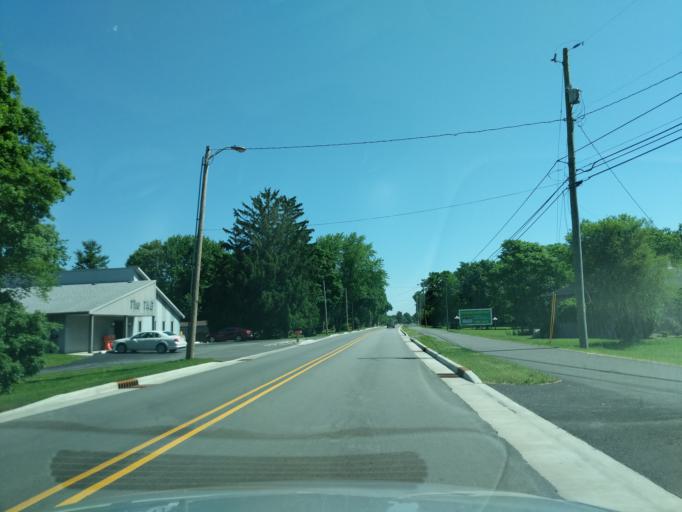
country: US
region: Indiana
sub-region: Huntington County
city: Huntington
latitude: 40.8625
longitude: -85.5066
